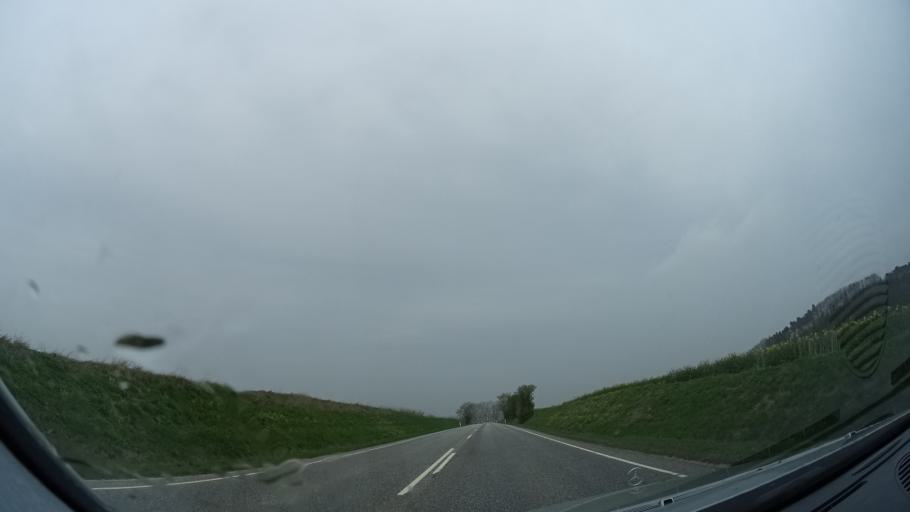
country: DK
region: Zealand
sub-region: Holbaek Kommune
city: Holbaek
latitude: 55.7505
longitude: 11.6215
